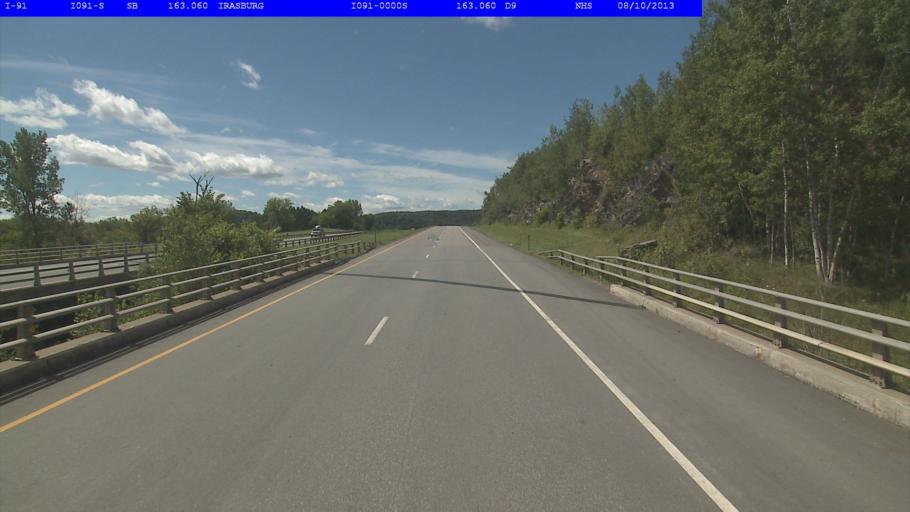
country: US
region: Vermont
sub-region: Orleans County
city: Newport
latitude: 44.8285
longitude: -72.2020
